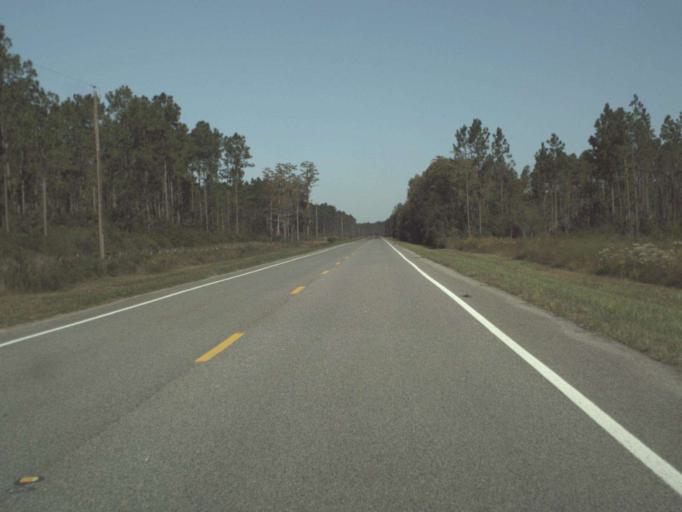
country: US
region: Florida
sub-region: Leon County
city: Woodville
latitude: 30.2733
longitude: -84.0422
